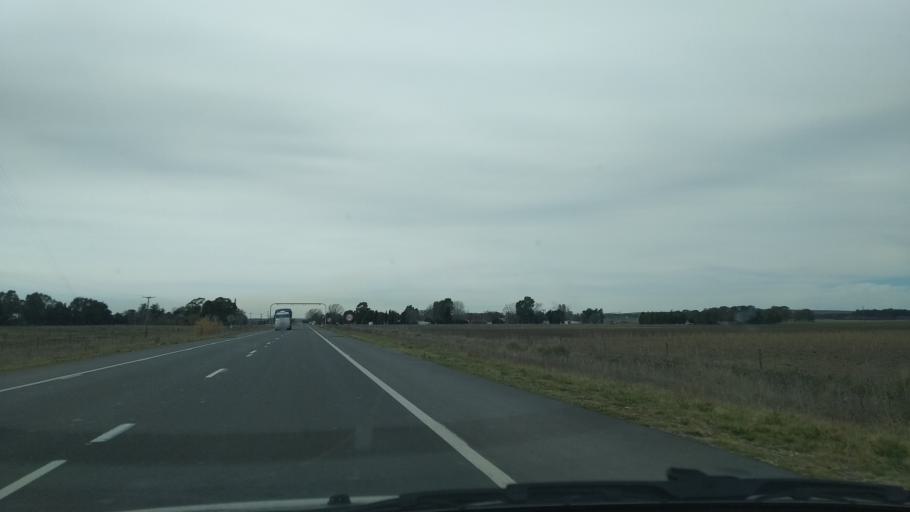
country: AR
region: Buenos Aires
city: Olavarria
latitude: -36.9917
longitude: -60.3186
